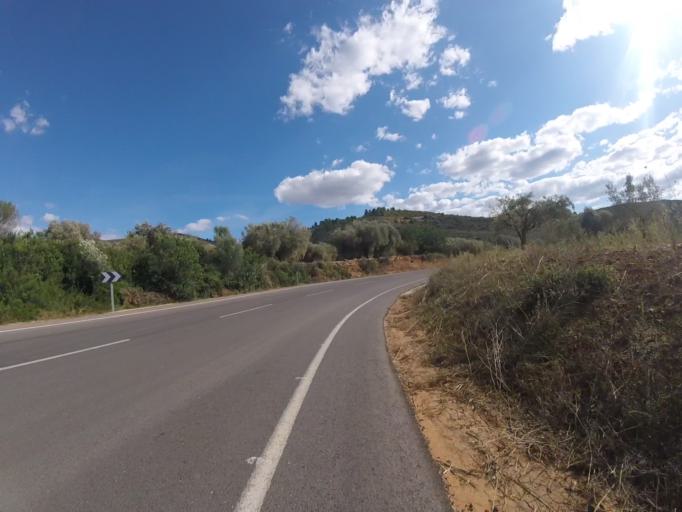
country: ES
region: Valencia
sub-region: Provincia de Castello
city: Cuevas de Vinroma
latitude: 40.3001
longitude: 0.1674
